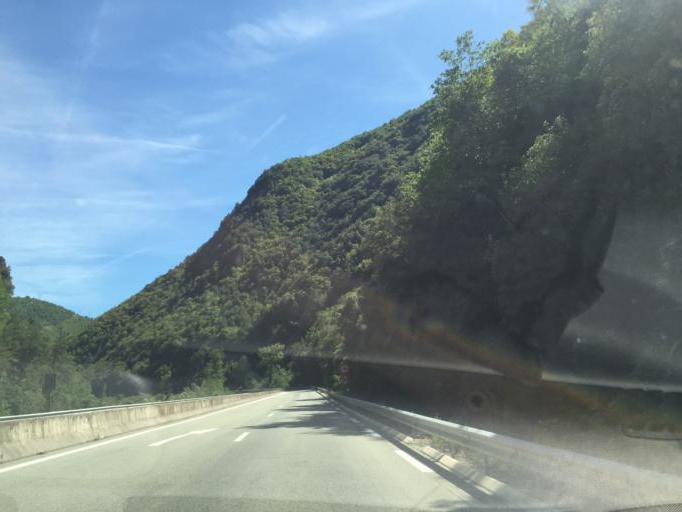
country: FR
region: Provence-Alpes-Cote d'Azur
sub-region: Departement des Alpes-Maritimes
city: Saint-Martin-Vesubie
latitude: 44.0125
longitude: 7.1315
